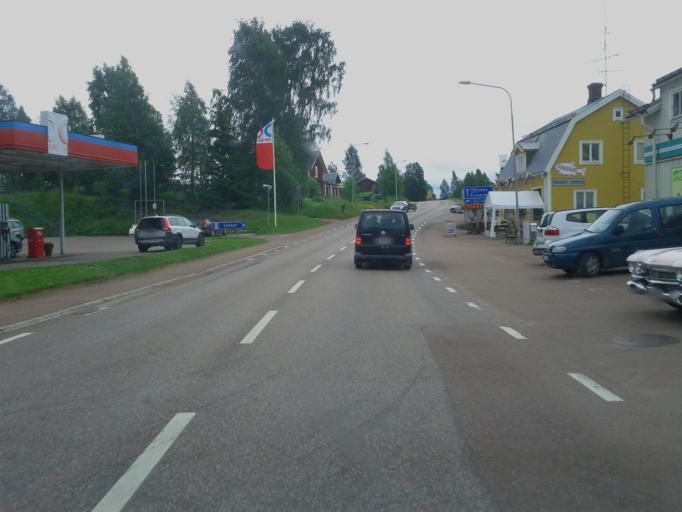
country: NO
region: Hedmark
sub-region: Trysil
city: Innbygda
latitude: 61.6932
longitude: 13.1412
